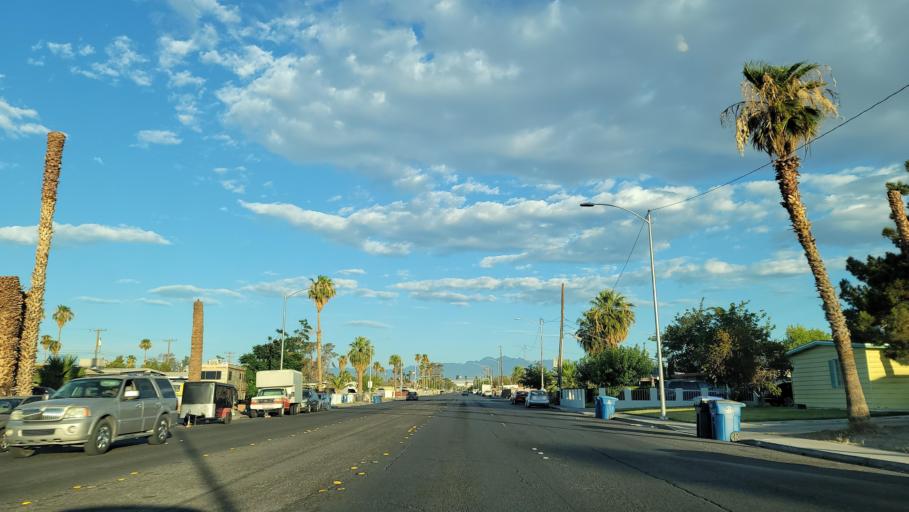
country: US
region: Nevada
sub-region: Clark County
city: North Las Vegas
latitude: 36.1883
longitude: -115.1047
